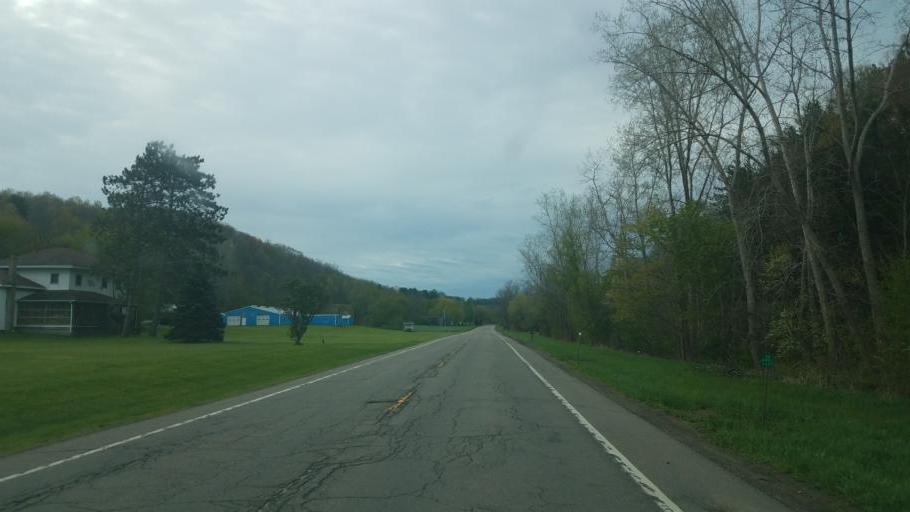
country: US
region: New York
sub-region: Steuben County
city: Canisteo
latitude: 42.2102
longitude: -77.5642
